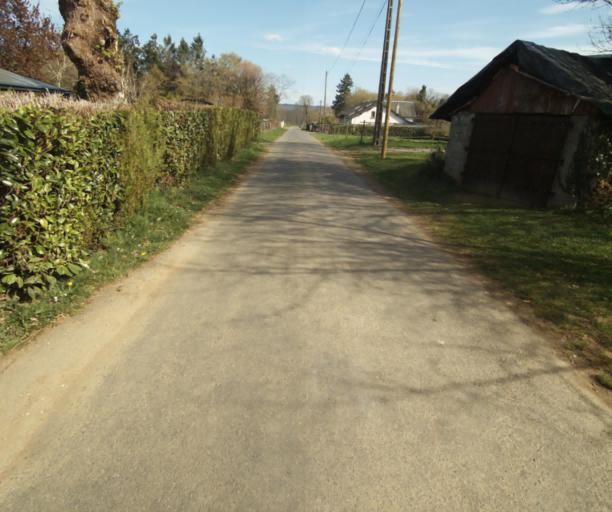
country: FR
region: Limousin
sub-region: Departement de la Correze
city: Naves
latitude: 45.3495
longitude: 1.7627
